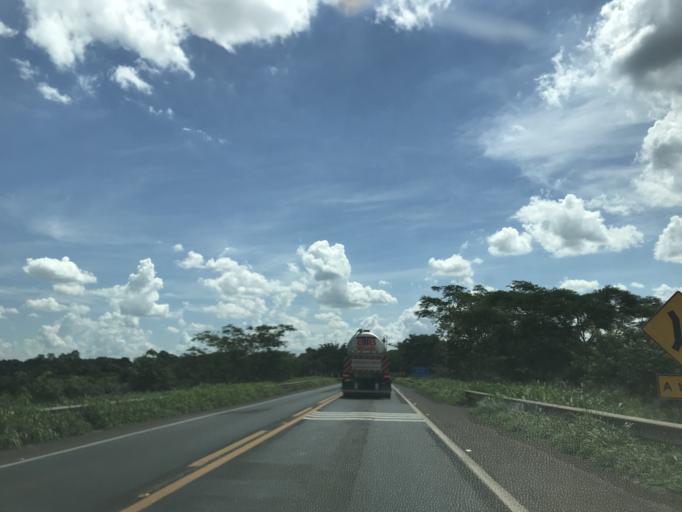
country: BR
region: Sao Paulo
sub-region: Nova Granada
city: Nova Granada
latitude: -20.4175
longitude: -49.2649
